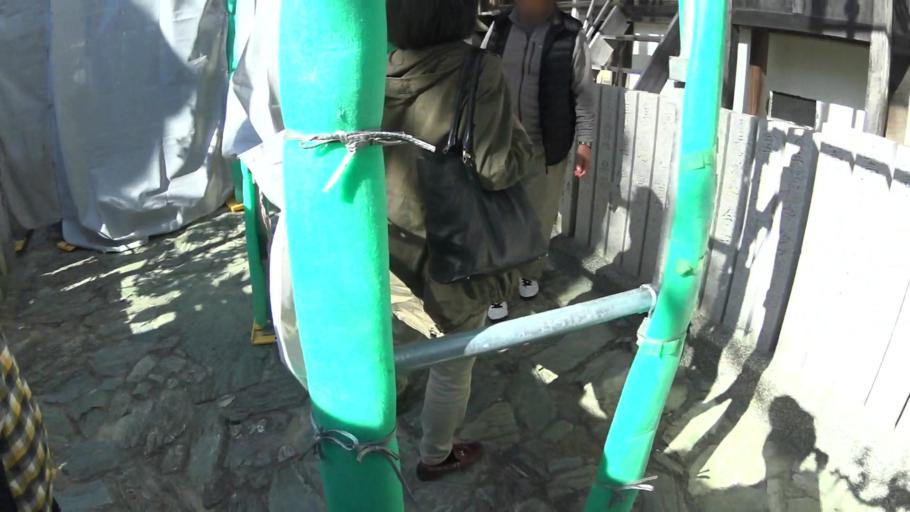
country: JP
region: Wakayama
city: Minato
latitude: 34.1911
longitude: 135.1437
